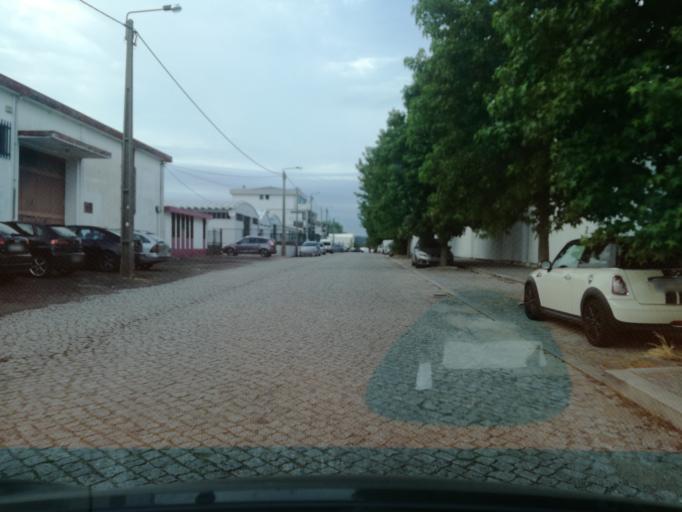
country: PT
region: Porto
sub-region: Maia
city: Anta
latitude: 41.2572
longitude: -8.6133
